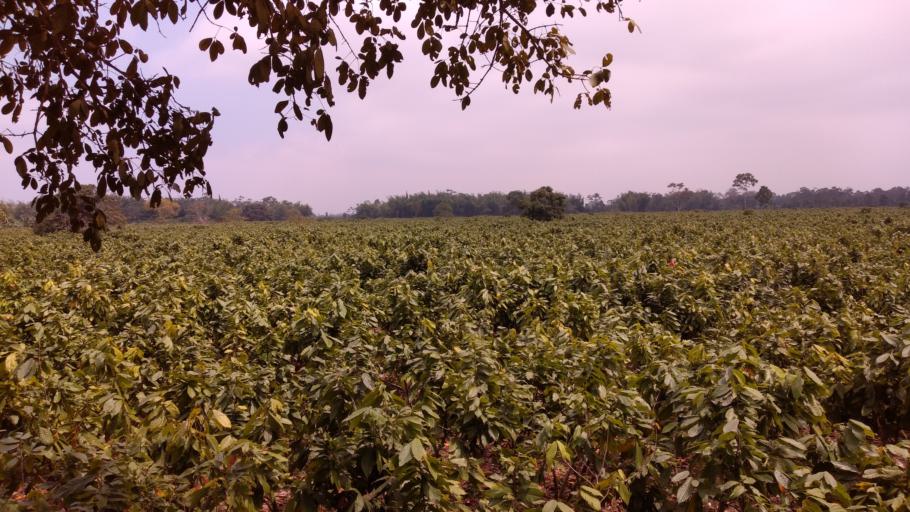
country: EC
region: Canar
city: La Troncal
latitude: -2.3768
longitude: -79.4116
